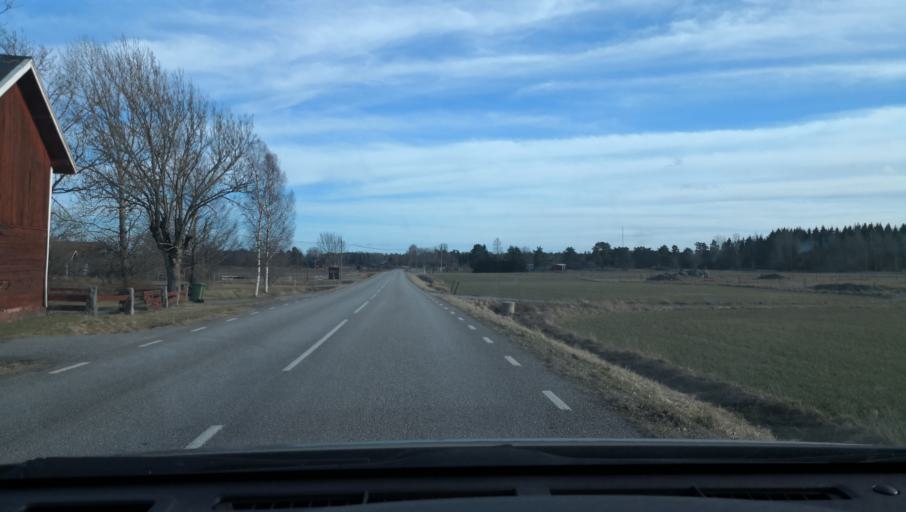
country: SE
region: Uppsala
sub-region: Enkopings Kommun
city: Enkoping
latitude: 59.6056
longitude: 17.1143
